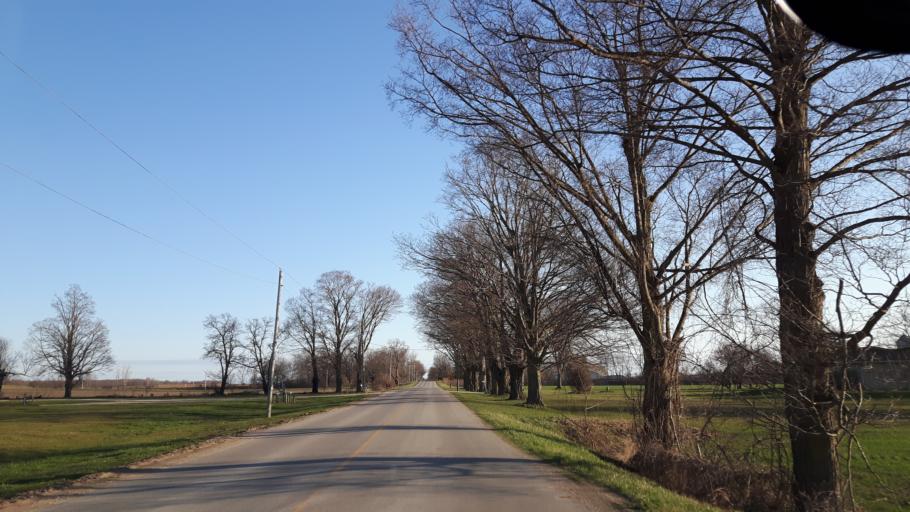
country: CA
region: Ontario
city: Goderich
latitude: 43.7036
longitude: -81.6850
